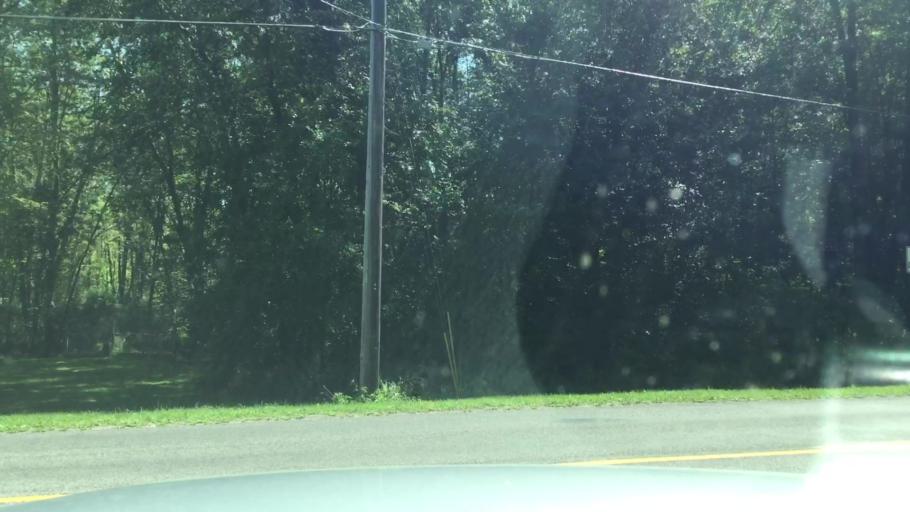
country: US
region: Michigan
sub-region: Lenawee County
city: Manitou Beach-Devils Lake
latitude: 41.9846
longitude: -84.2808
